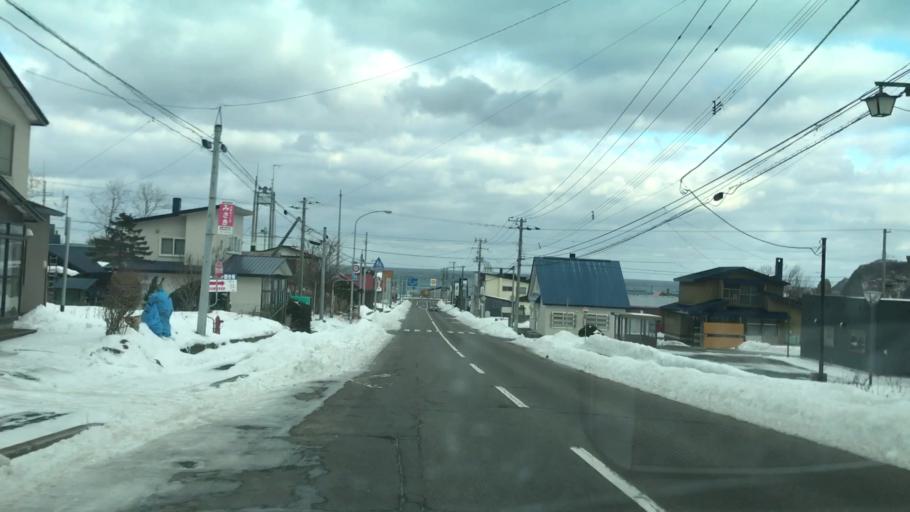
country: JP
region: Hokkaido
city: Yoichi
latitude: 43.3404
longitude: 140.4584
